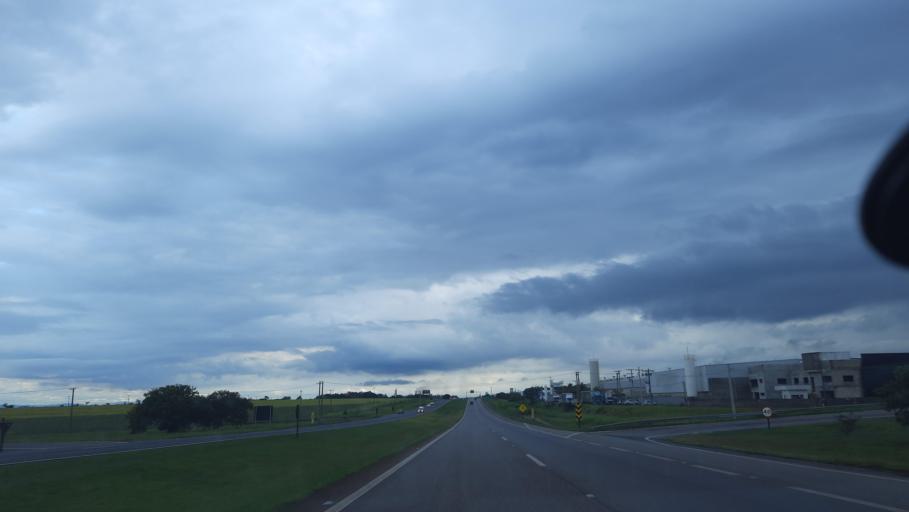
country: BR
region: Sao Paulo
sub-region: Moji-Guacu
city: Mogi-Gaucu
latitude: -22.2943
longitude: -46.9701
